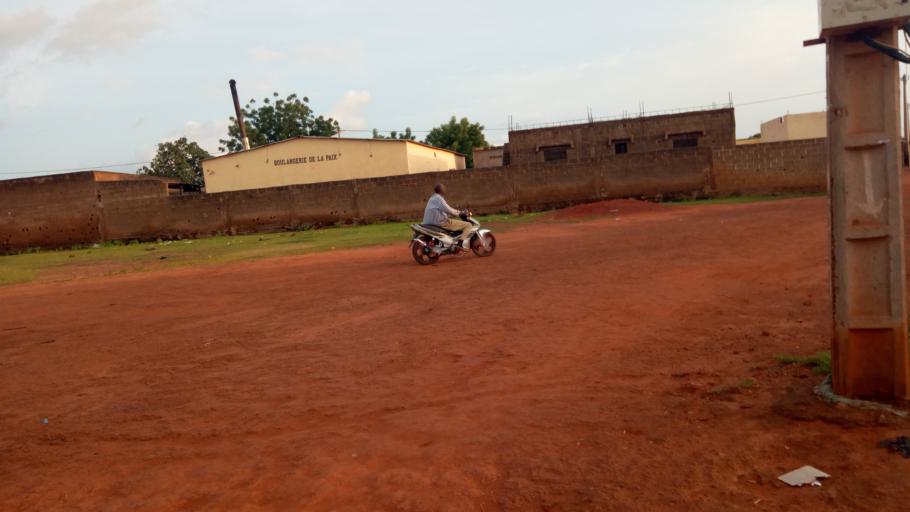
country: ML
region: Sikasso
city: Koutiala
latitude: 12.3748
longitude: -5.4850
